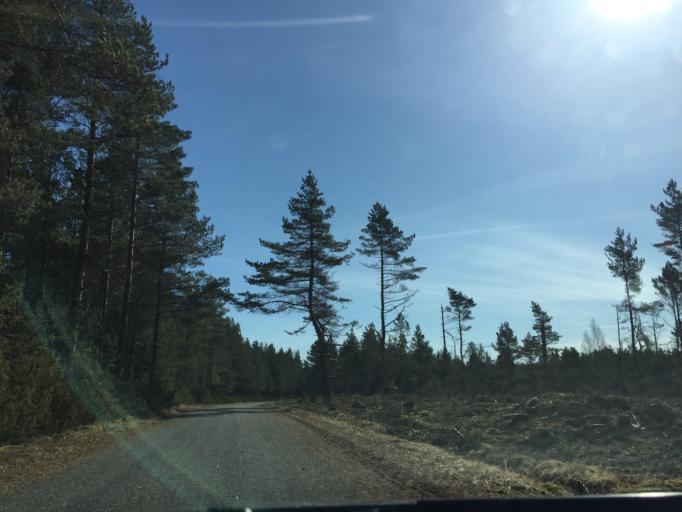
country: EE
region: Laeaene
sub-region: Lihula vald
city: Lihula
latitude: 58.6132
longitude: 23.5652
